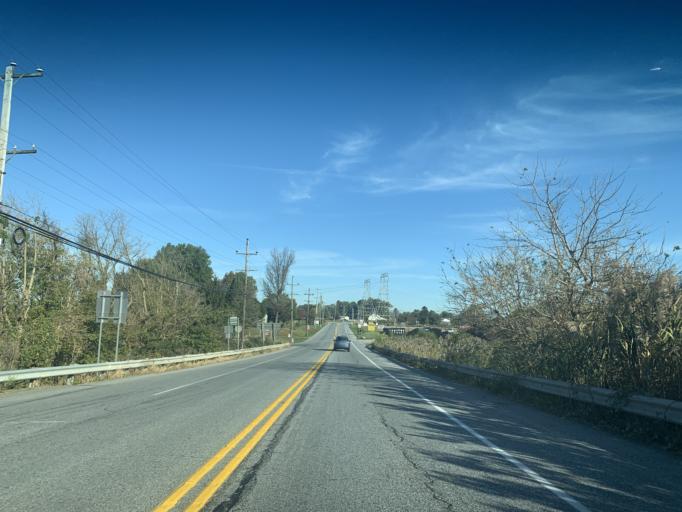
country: US
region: Pennsylvania
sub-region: Chester County
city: Oxford
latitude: 39.8086
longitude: -75.9671
